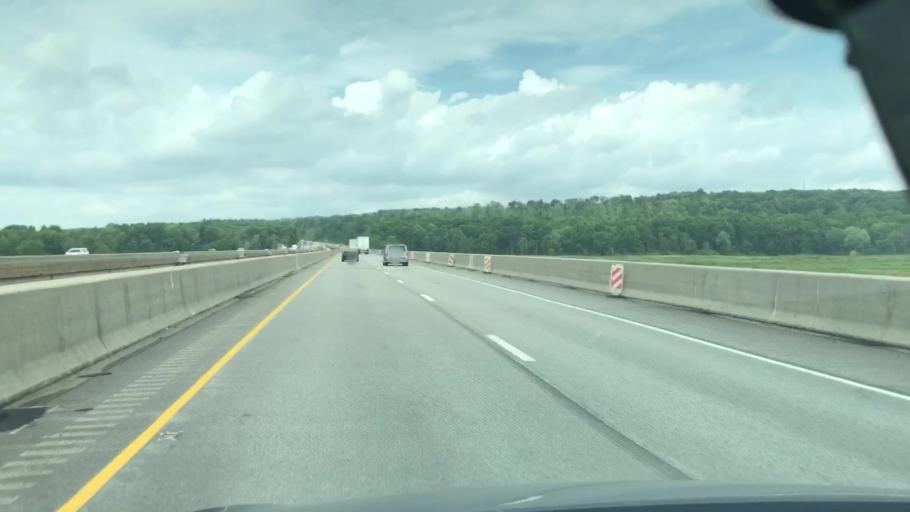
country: US
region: Pennsylvania
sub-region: Crawford County
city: Meadville
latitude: 41.5435
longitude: -80.1829
